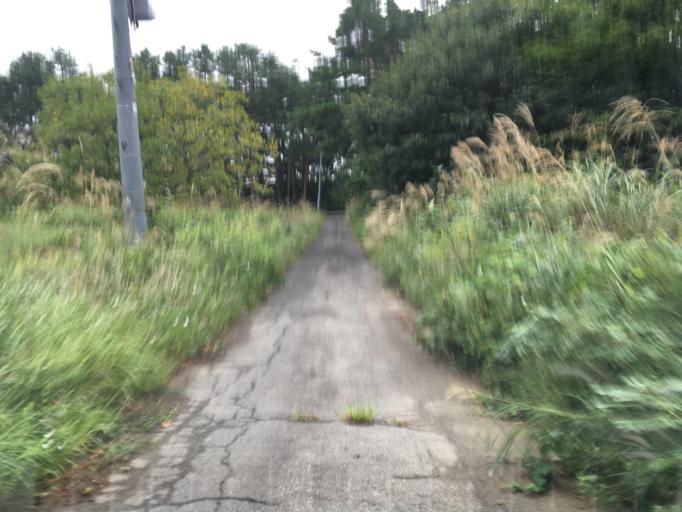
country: JP
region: Fukushima
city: Fukushima-shi
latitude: 37.8089
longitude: 140.3439
